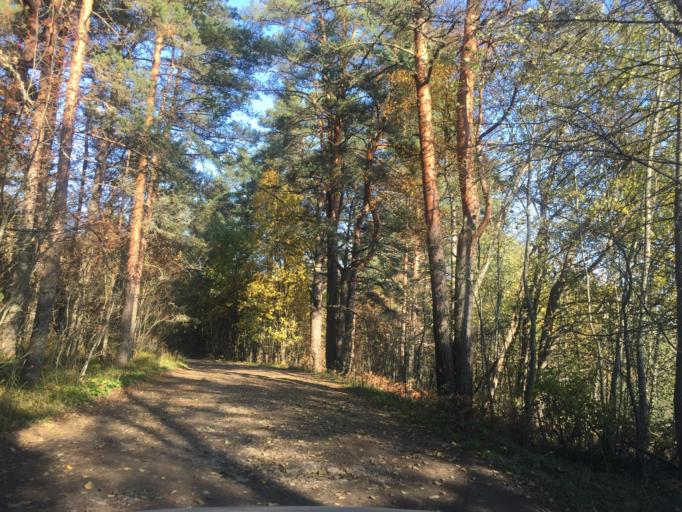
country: RU
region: Leningrad
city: Kuznechnoye
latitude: 61.2954
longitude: 30.0598
